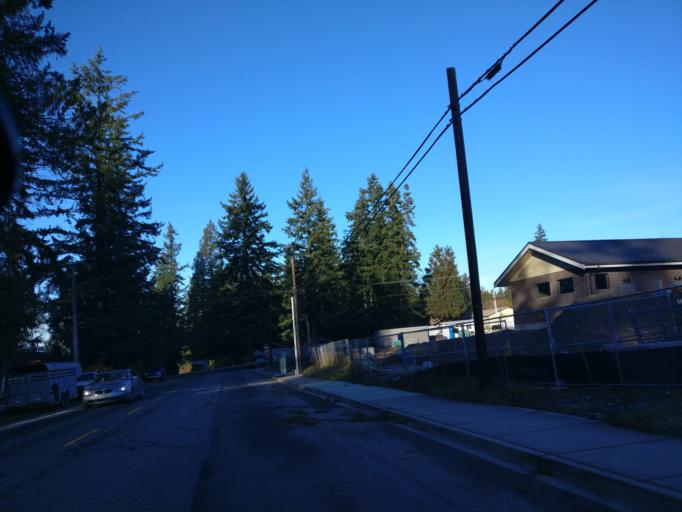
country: US
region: Washington
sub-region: Skagit County
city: Mount Vernon
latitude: 48.4201
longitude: -122.2971
